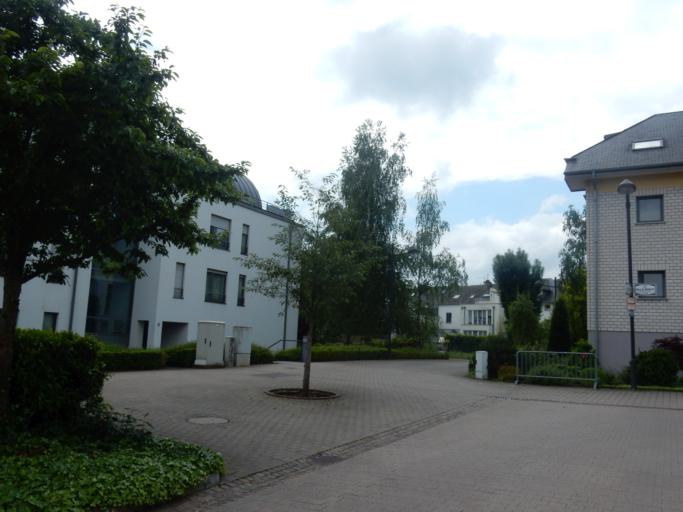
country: LU
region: Luxembourg
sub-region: Canton de Luxembourg
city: Strassen
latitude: 49.6065
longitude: 6.0993
